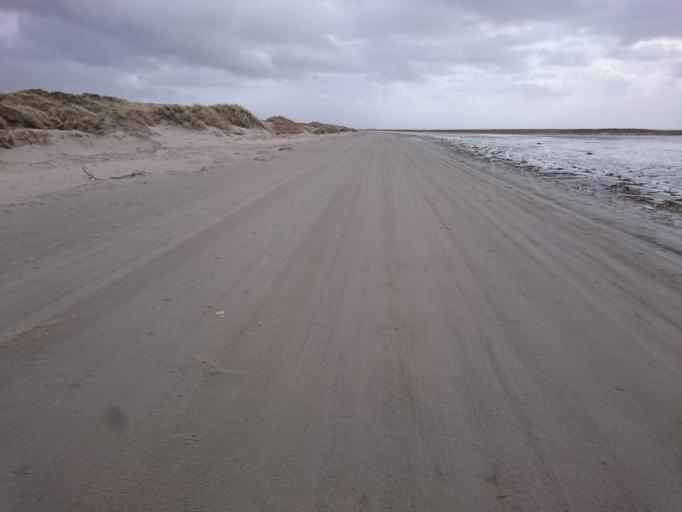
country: DK
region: South Denmark
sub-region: Fano Kommune
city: Nordby
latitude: 55.4301
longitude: 8.3657
